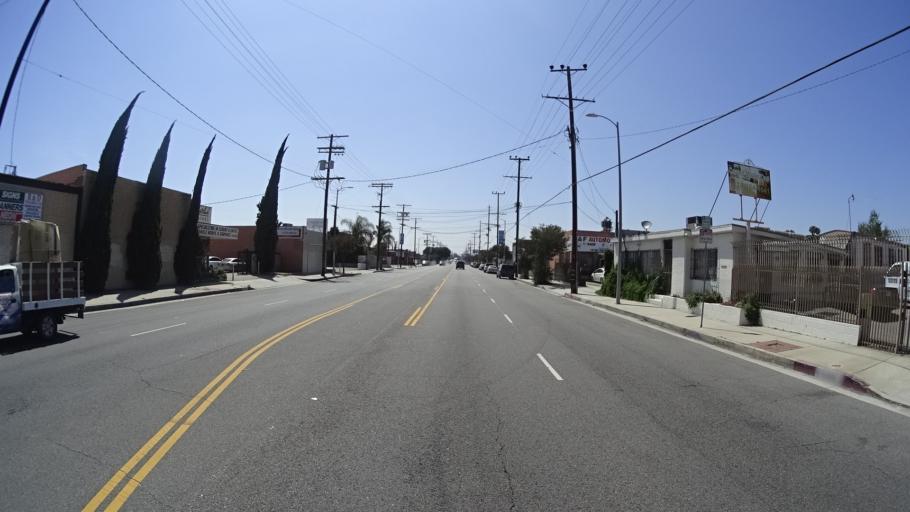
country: US
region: California
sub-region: Los Angeles County
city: Van Nuys
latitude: 34.2075
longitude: -118.4186
